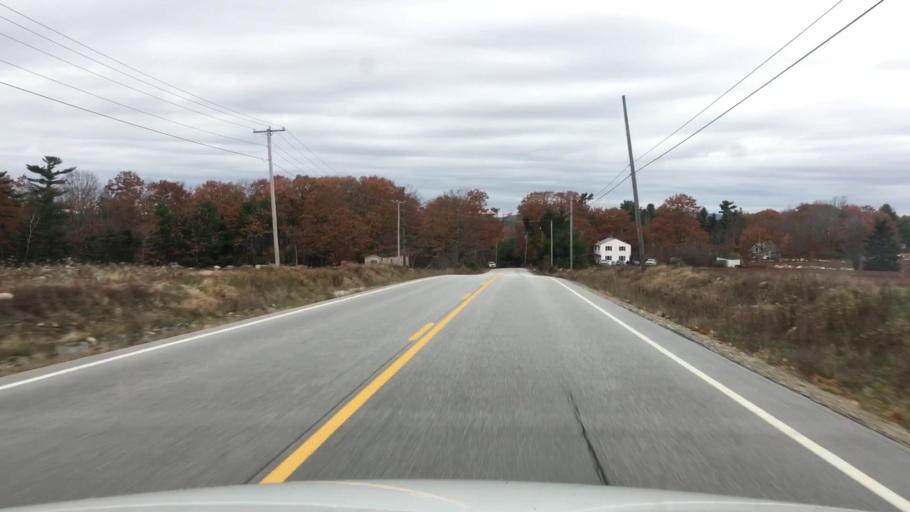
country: US
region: Maine
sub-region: Hancock County
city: Orland
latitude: 44.5529
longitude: -68.6936
